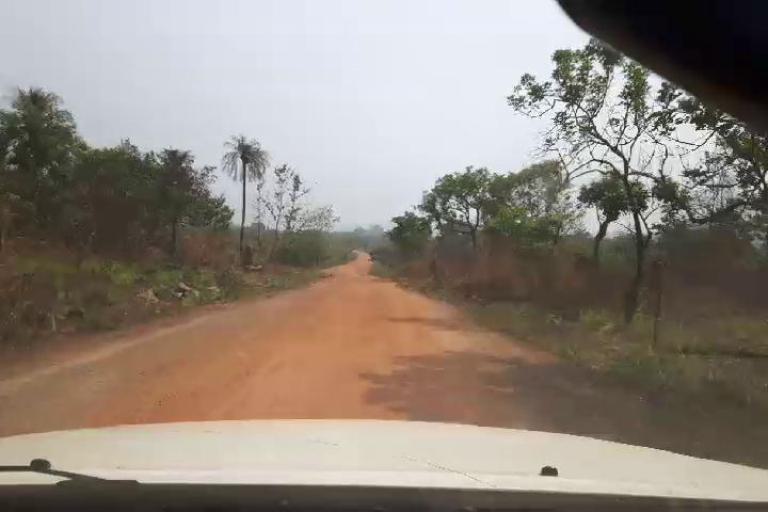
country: SL
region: Northern Province
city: Bumbuna
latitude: 8.9570
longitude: -11.8042
